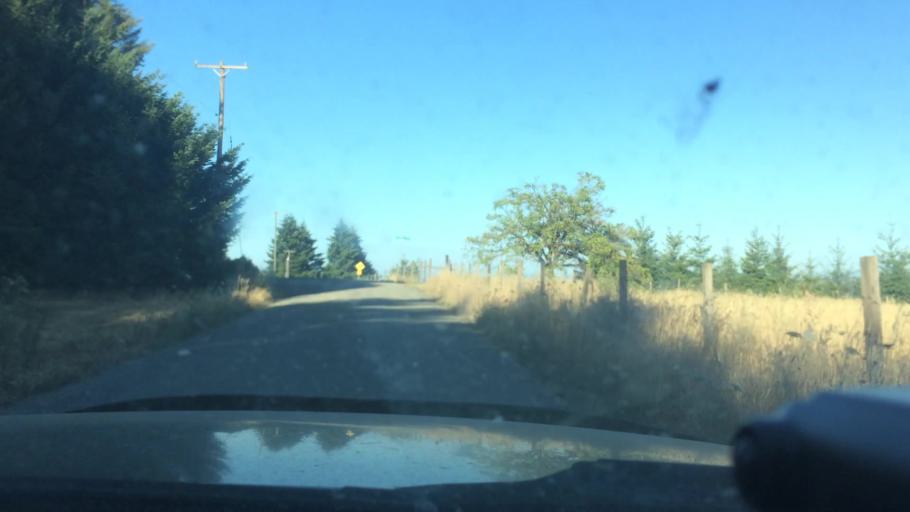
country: US
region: Oregon
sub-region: Yamhill County
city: Newberg
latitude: 45.3709
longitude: -122.9762
